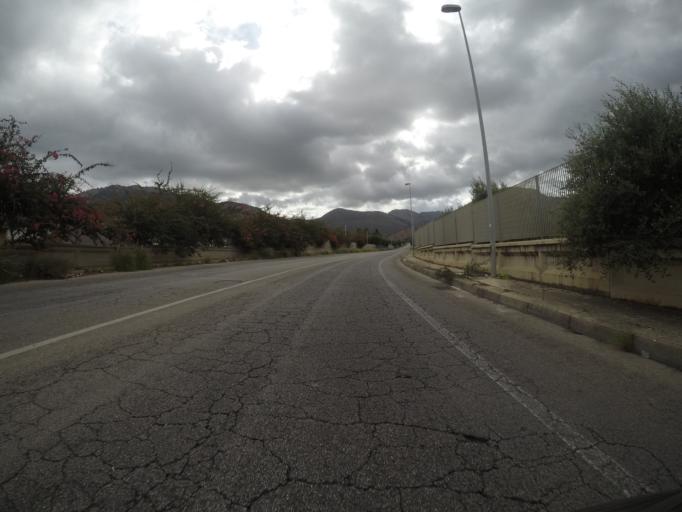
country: IT
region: Sicily
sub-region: Palermo
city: Capaci
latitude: 38.1725
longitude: 13.2191
